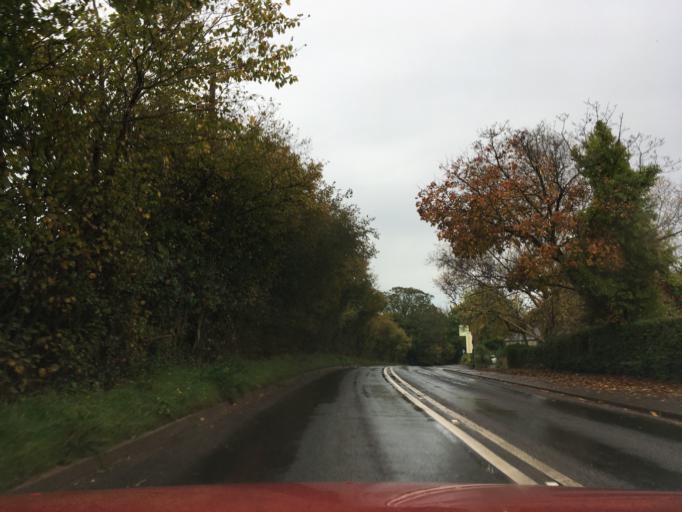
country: GB
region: Wales
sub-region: Newport
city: Bishton
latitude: 51.6018
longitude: -2.8788
